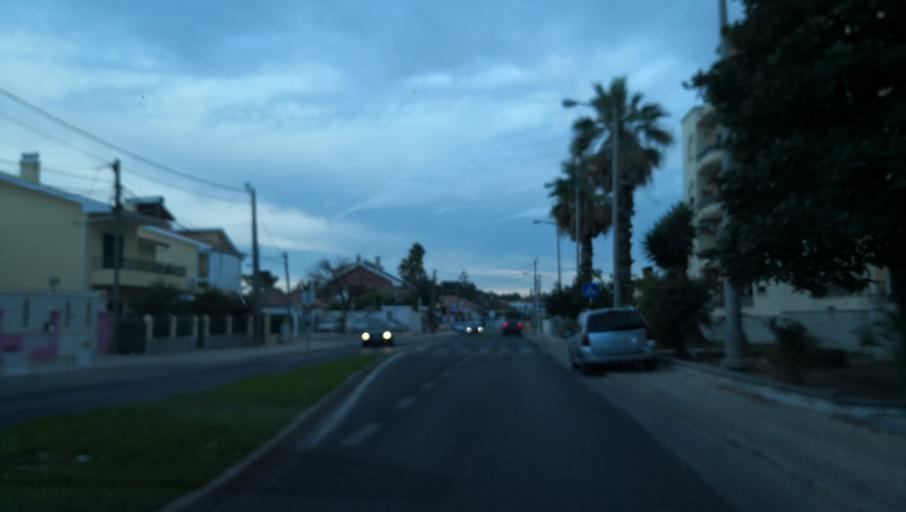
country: PT
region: Setubal
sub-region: Almada
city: Charneca
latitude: 38.6089
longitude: -9.1877
